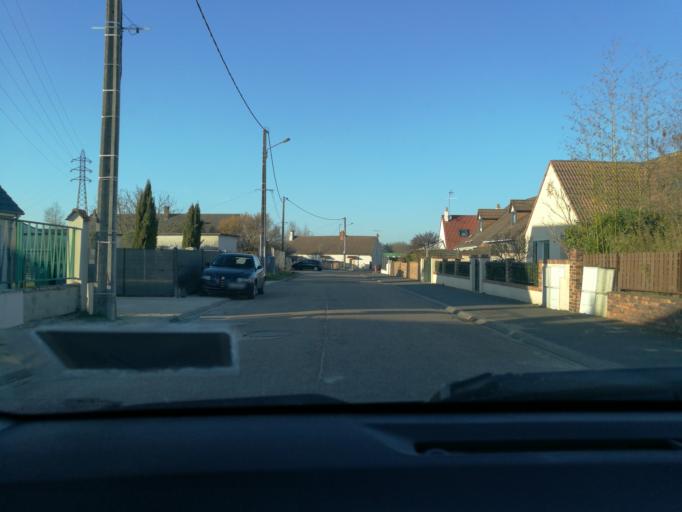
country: FR
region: Centre
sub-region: Departement du Loiret
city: Semoy
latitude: 47.9398
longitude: 1.9388
